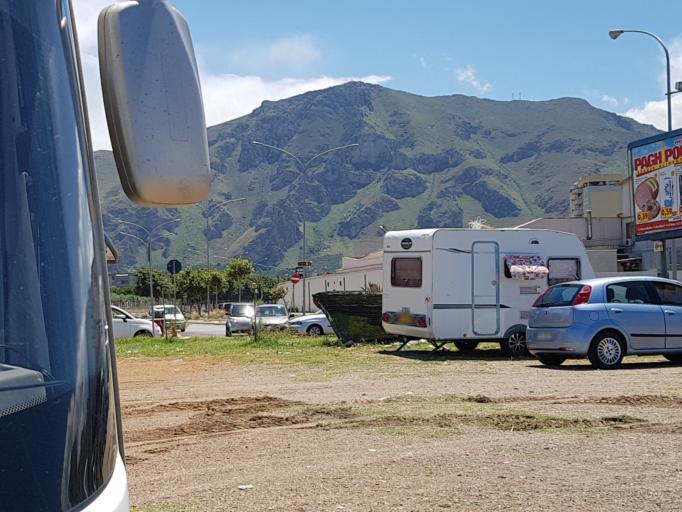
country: IT
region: Sicily
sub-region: Palermo
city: Ciaculli
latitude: 38.0978
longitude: 13.4144
